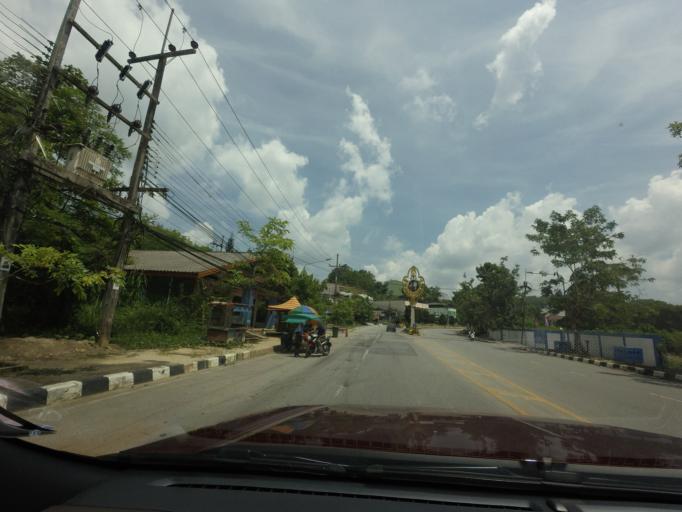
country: TH
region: Yala
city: Betong
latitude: 5.7734
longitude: 101.0639
